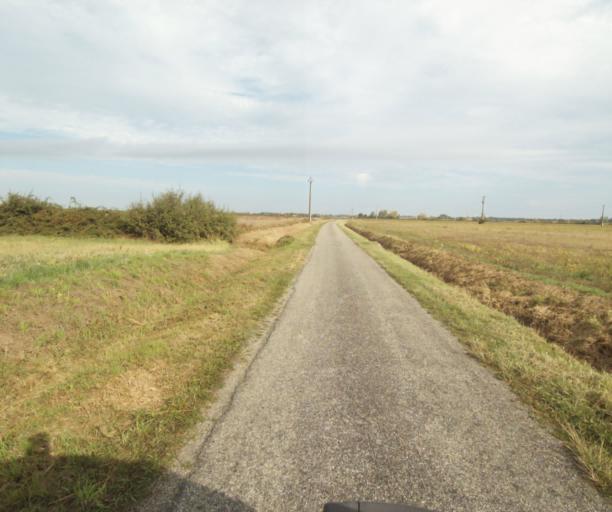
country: FR
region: Midi-Pyrenees
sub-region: Departement du Tarn-et-Garonne
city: Finhan
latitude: 43.9309
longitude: 1.2250
